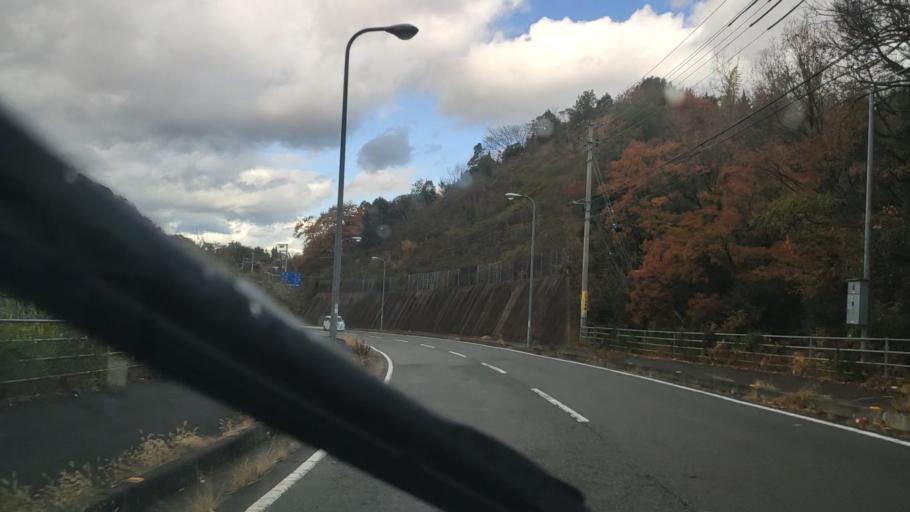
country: JP
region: Tokushima
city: Kamojimacho-jogejima
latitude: 34.2253
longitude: 134.3886
